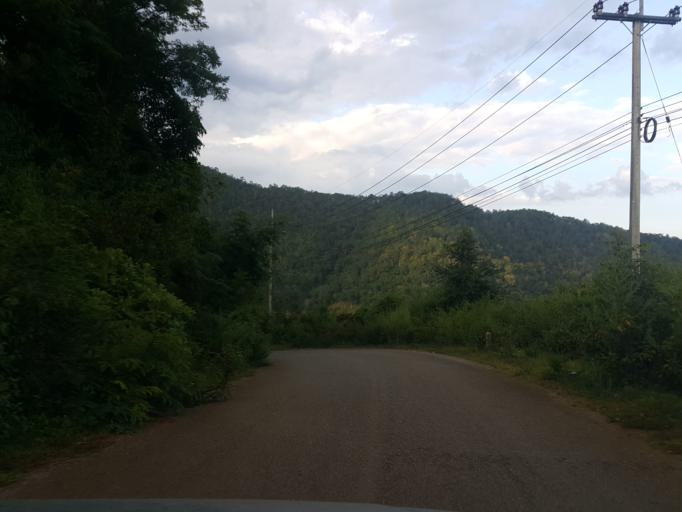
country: TH
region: Mae Hong Son
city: Khun Yuam
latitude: 18.7461
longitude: 98.2010
